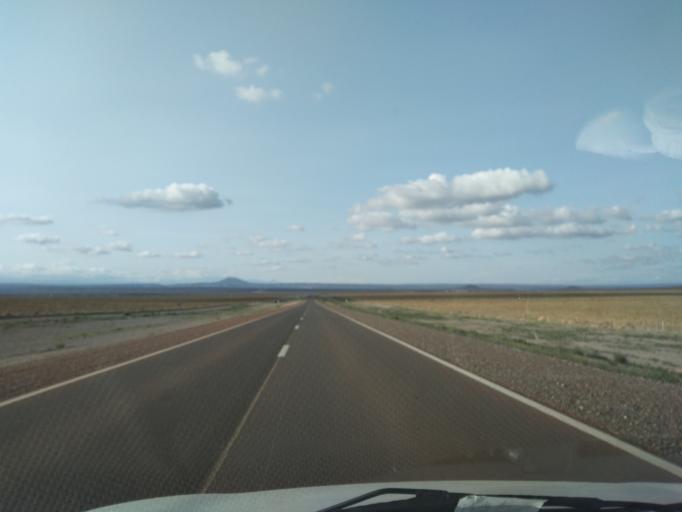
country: AR
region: Mendoza
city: San Rafael
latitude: -34.6789
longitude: -69.1587
